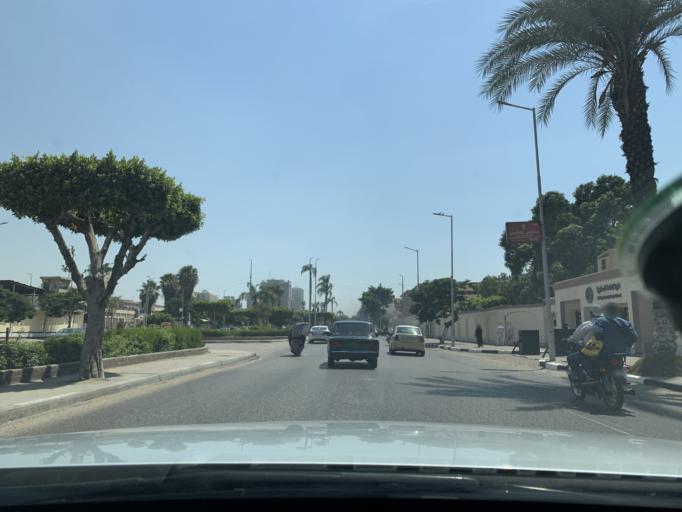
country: EG
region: Muhafazat al Qahirah
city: Cairo
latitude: 30.0792
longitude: 31.2905
